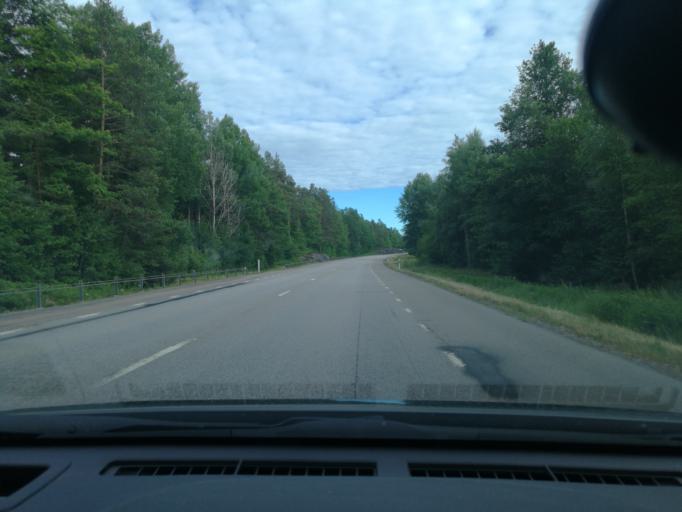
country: SE
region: Kalmar
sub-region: Vasterviks Kommun
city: Ankarsrum
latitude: 57.6204
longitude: 16.4658
